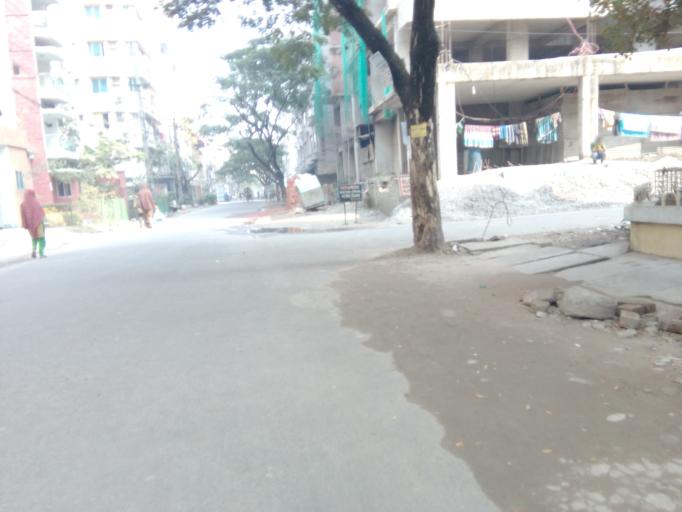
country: BD
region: Dhaka
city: Tungi
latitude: 23.8183
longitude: 90.4281
